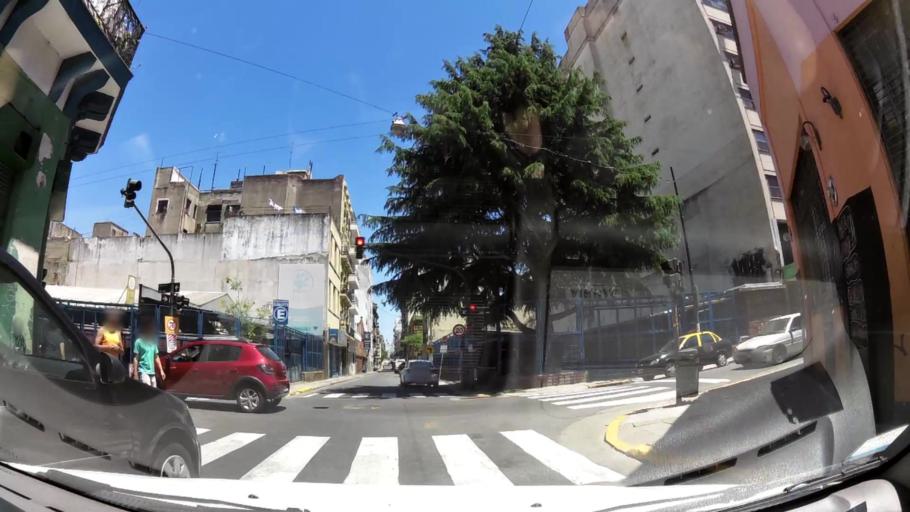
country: AR
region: Buenos Aires F.D.
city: Buenos Aires
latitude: -34.6139
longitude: -58.3760
